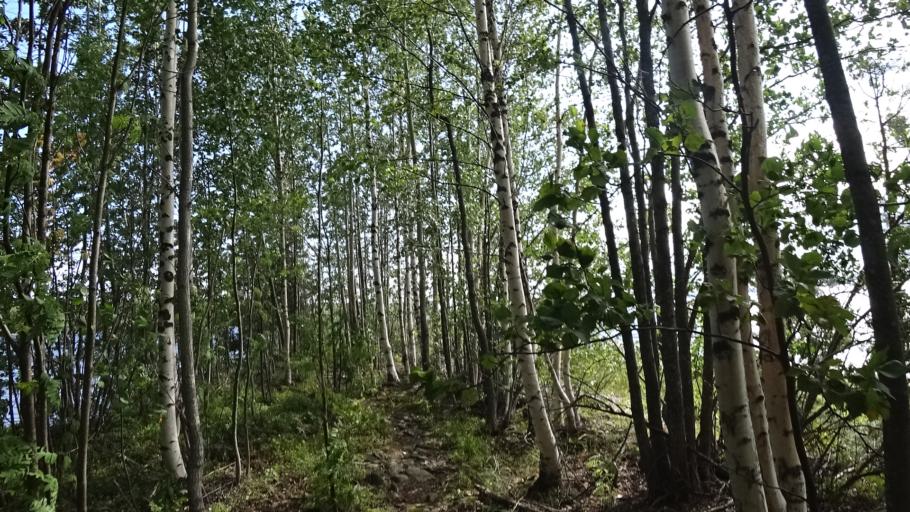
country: FI
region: North Karelia
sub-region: Keski-Karjala
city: Raeaekkylae
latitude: 62.3941
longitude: 29.7594
